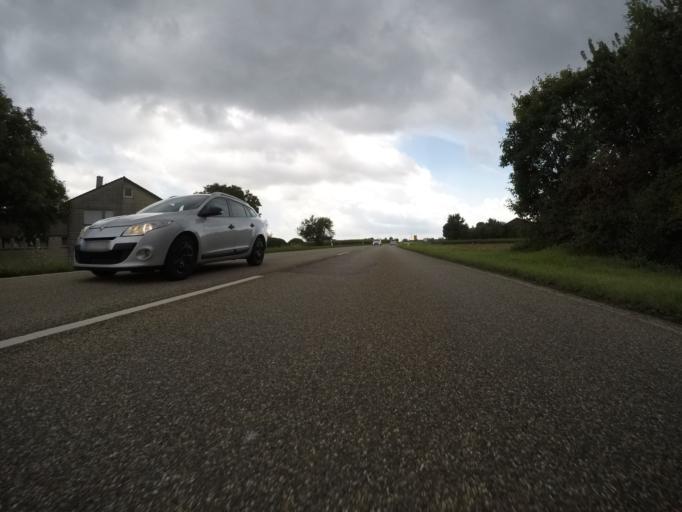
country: DE
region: Baden-Wuerttemberg
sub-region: Regierungsbezirk Stuttgart
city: Markgroningen
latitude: 48.8945
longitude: 9.0880
